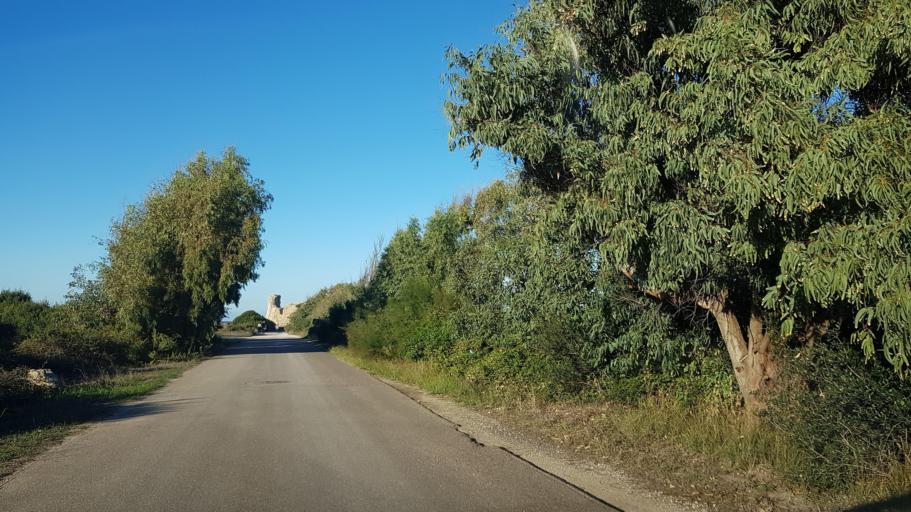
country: IT
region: Apulia
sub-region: Provincia di Lecce
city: Giorgilorio
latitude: 40.4580
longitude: 18.2130
